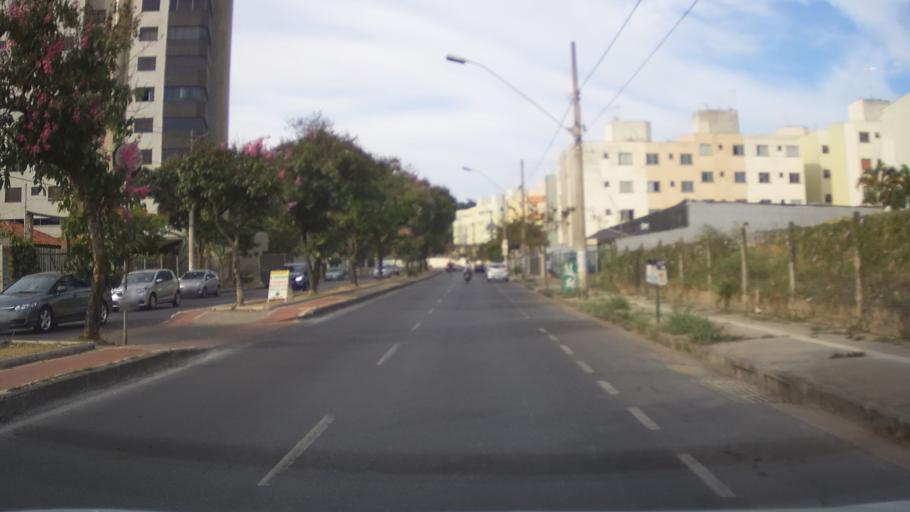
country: BR
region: Minas Gerais
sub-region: Belo Horizonte
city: Belo Horizonte
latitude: -19.8647
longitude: -43.9835
